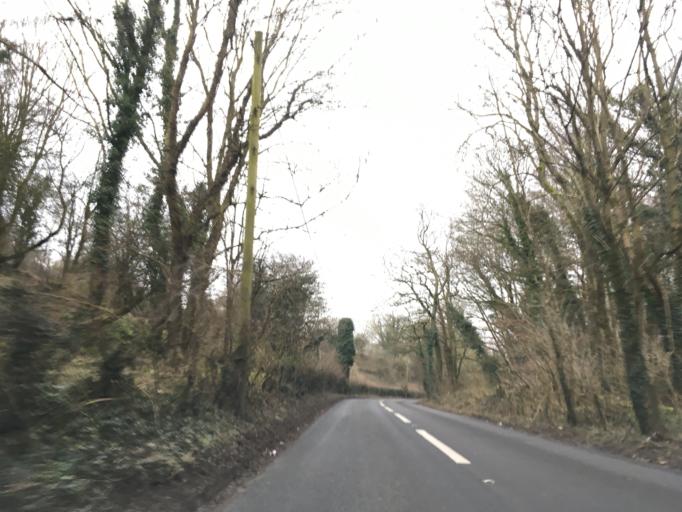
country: GB
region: England
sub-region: South Gloucestershire
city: Hinton
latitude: 51.5018
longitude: -2.3622
